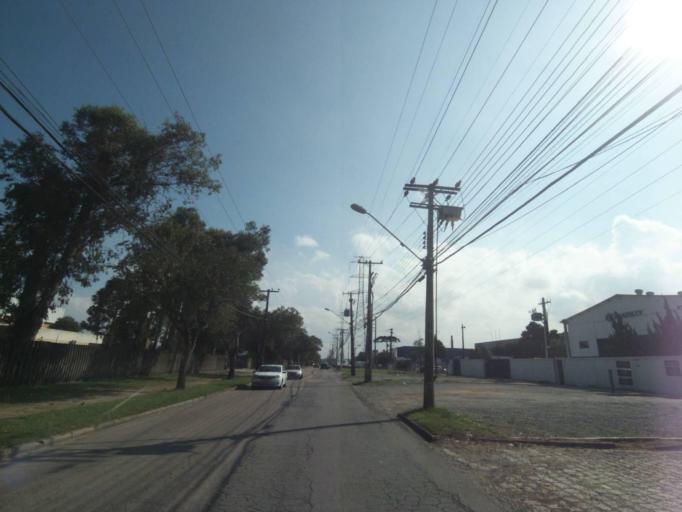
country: BR
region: Parana
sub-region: Araucaria
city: Araucaria
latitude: -25.5301
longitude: -49.3278
